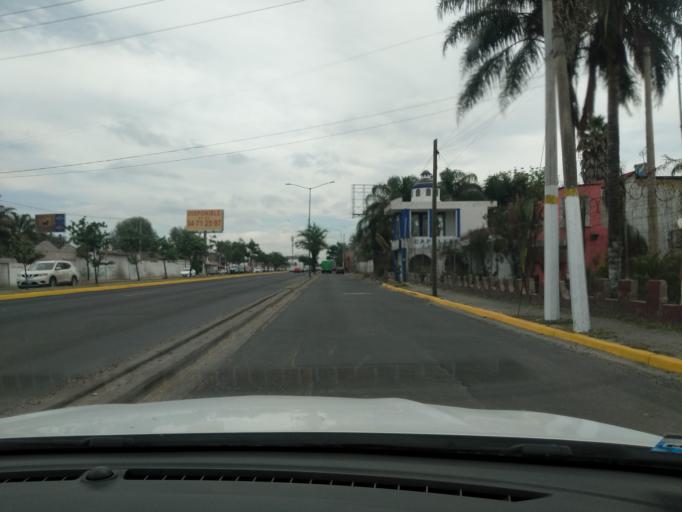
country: MX
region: Jalisco
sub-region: Zapopan
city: La Cuchilla (Extramuros de Tesistan)
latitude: 20.7734
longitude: -103.4519
